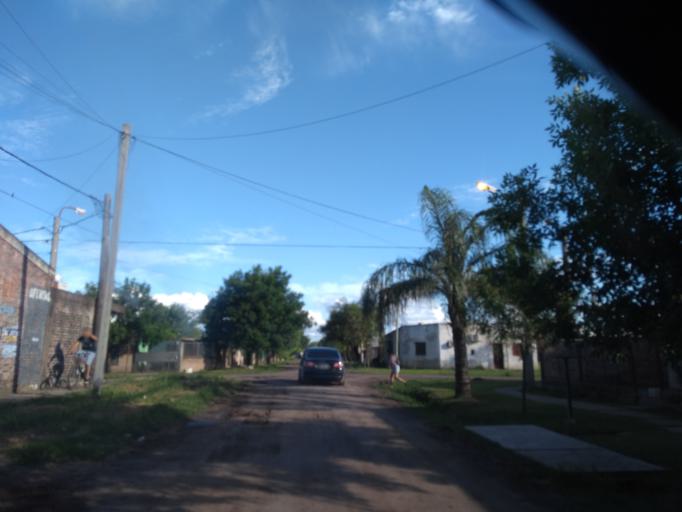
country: AR
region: Chaco
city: Fontana
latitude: -27.4123
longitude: -59.0385
